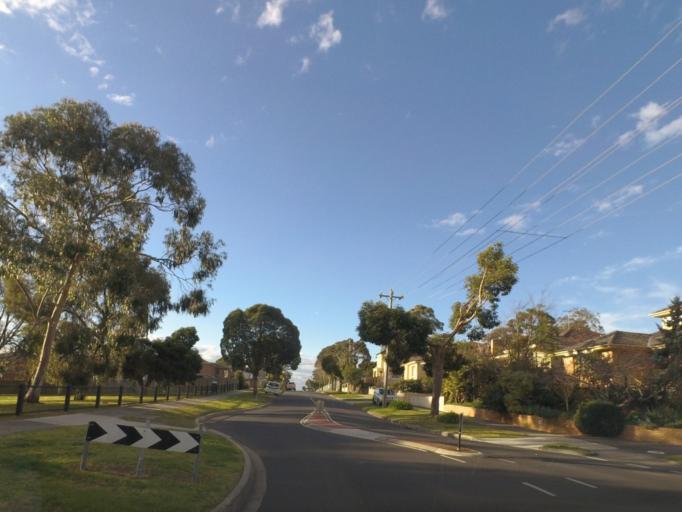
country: AU
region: Victoria
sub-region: Boroondara
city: Balwyn North
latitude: -37.7903
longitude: 145.0857
